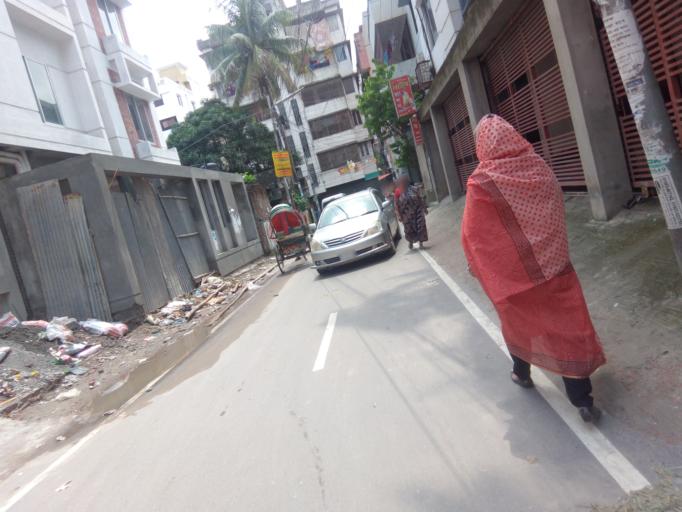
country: BD
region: Dhaka
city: Azimpur
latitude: 23.7645
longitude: 90.3614
